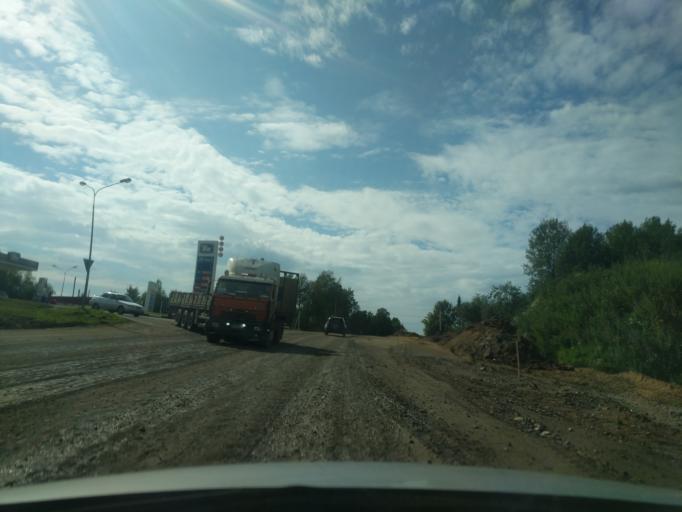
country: RU
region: Kostroma
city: Sudislavl'
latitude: 57.8752
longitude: 41.6749
